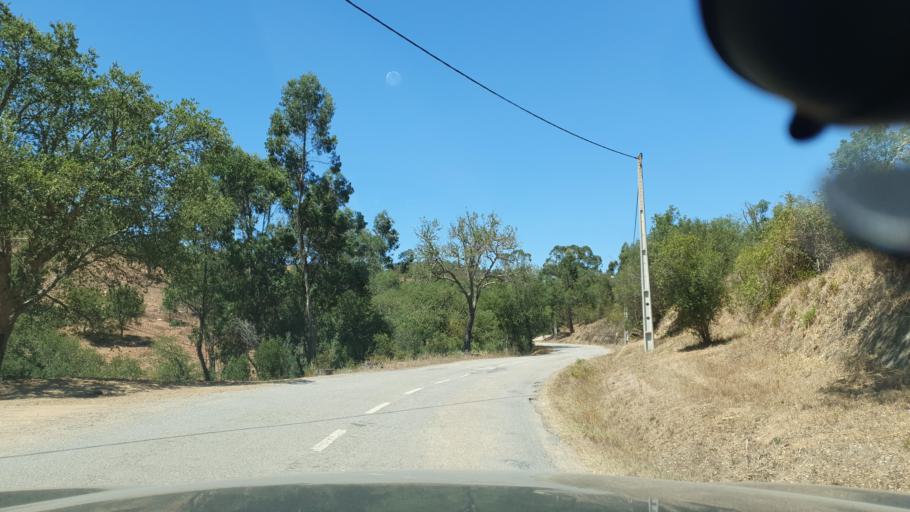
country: PT
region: Beja
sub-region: Odemira
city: Odemira
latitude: 37.5896
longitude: -8.4920
